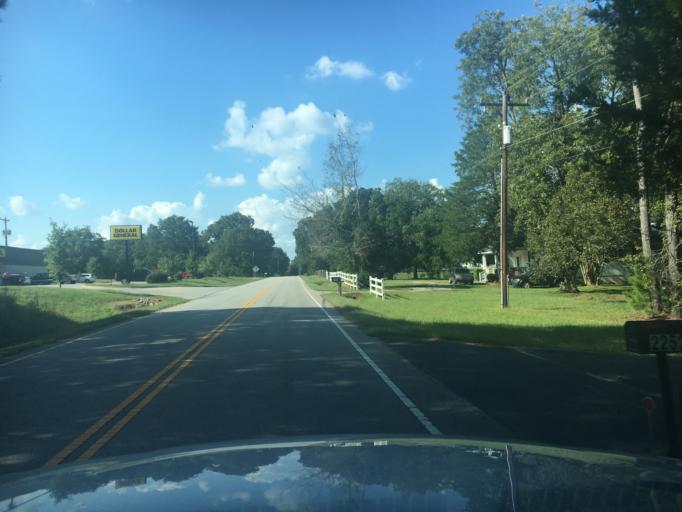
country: US
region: South Carolina
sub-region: Greenville County
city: Fountain Inn
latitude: 34.6126
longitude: -82.2353
